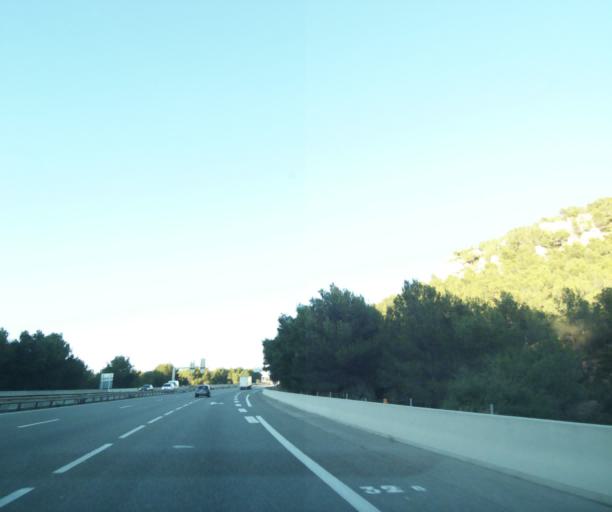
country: FR
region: Provence-Alpes-Cote d'Azur
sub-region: Departement des Bouches-du-Rhone
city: Roquefort-la-Bedoule
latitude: 43.2207
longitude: 5.5812
